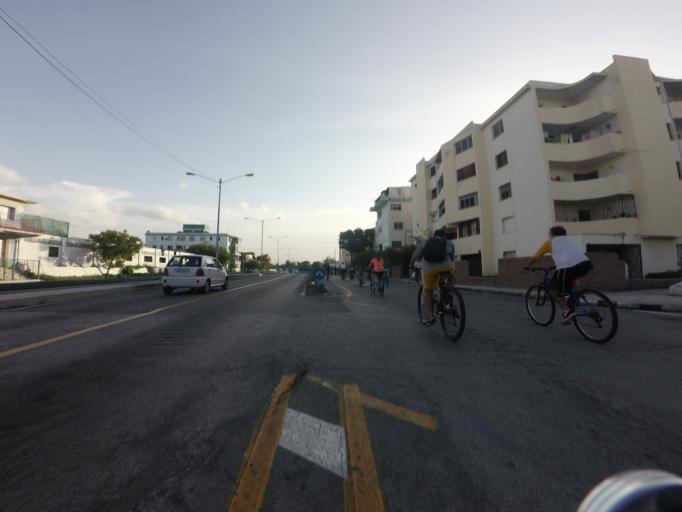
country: CU
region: La Habana
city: Havana
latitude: 23.1305
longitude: -82.4085
